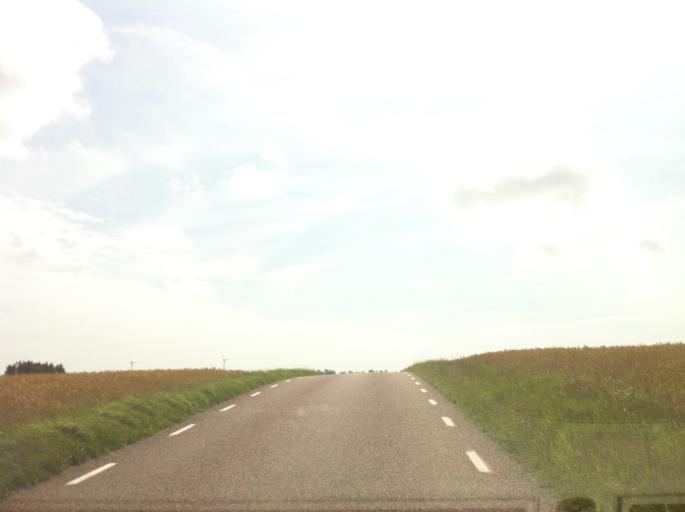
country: SE
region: Skane
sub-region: Skurups Kommun
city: Skurup
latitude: 55.4326
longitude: 13.4508
